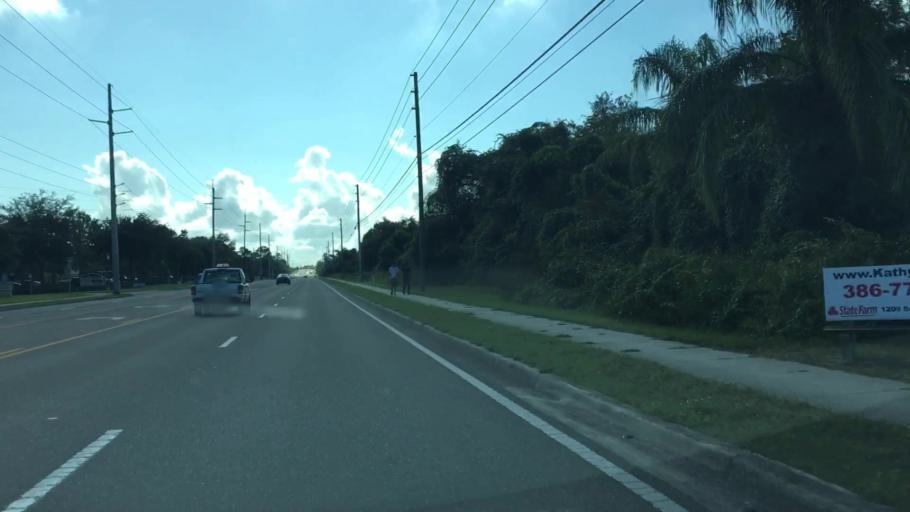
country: US
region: Florida
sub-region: Volusia County
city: Deltona
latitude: 28.8974
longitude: -81.2848
